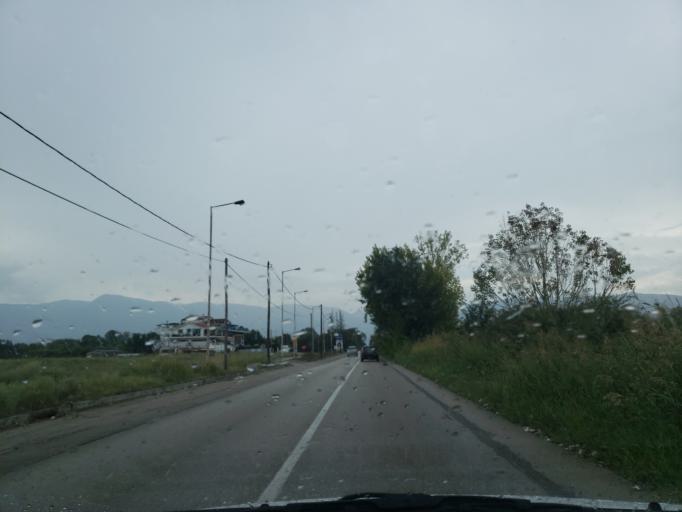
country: GR
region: Central Greece
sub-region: Nomos Fthiotidos
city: Anthili
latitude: 38.8532
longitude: 22.4404
